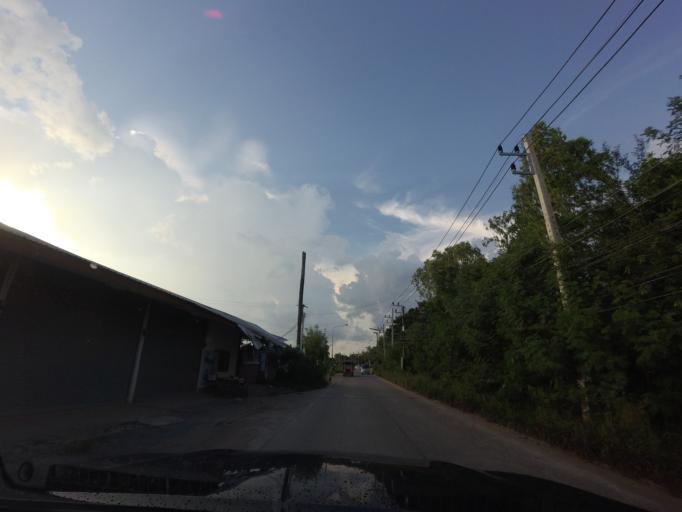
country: TH
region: Khon Kaen
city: Khon Kaen
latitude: 16.4029
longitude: 102.8650
